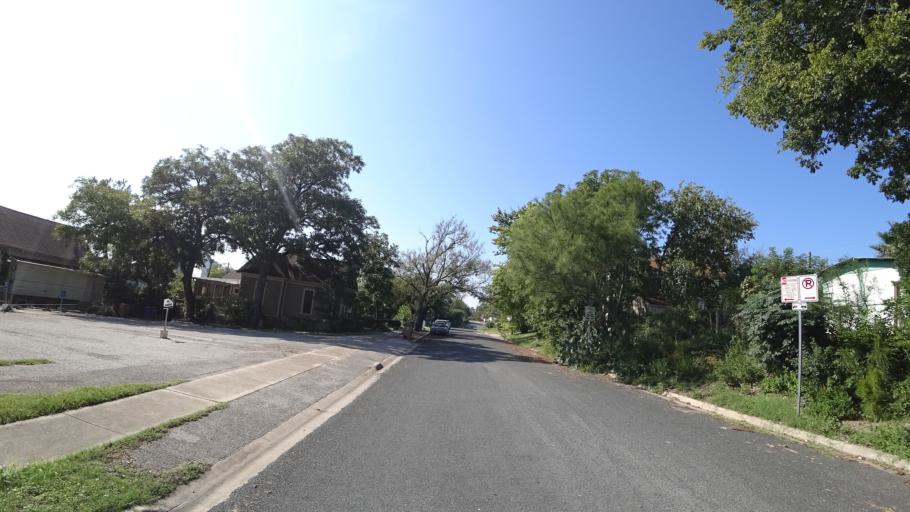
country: US
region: Texas
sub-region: Travis County
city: Austin
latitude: 30.2655
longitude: -97.7277
